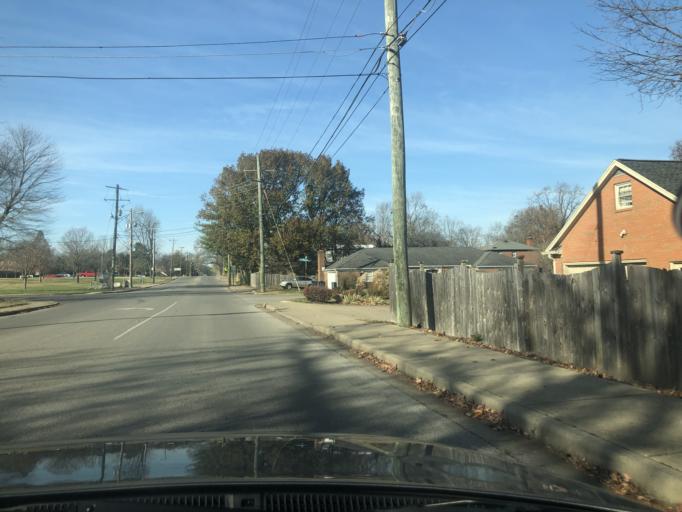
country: US
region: Indiana
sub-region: Warrick County
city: Newburgh
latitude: 37.9695
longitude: -87.4620
